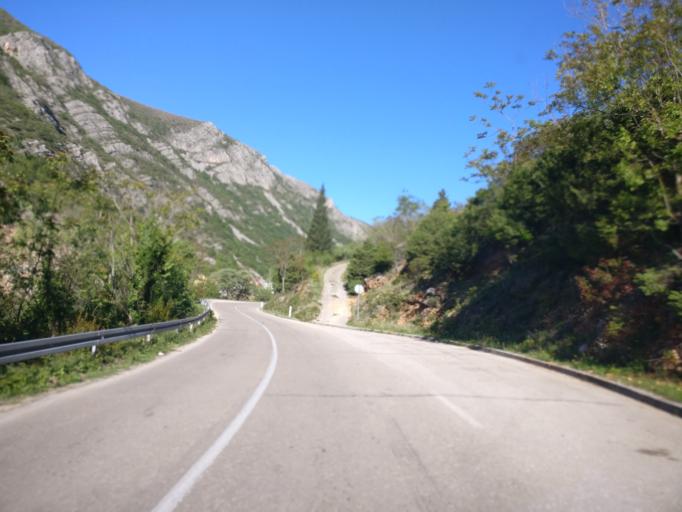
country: BA
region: Federation of Bosnia and Herzegovina
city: Stolac
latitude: 43.0777
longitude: 18.0214
